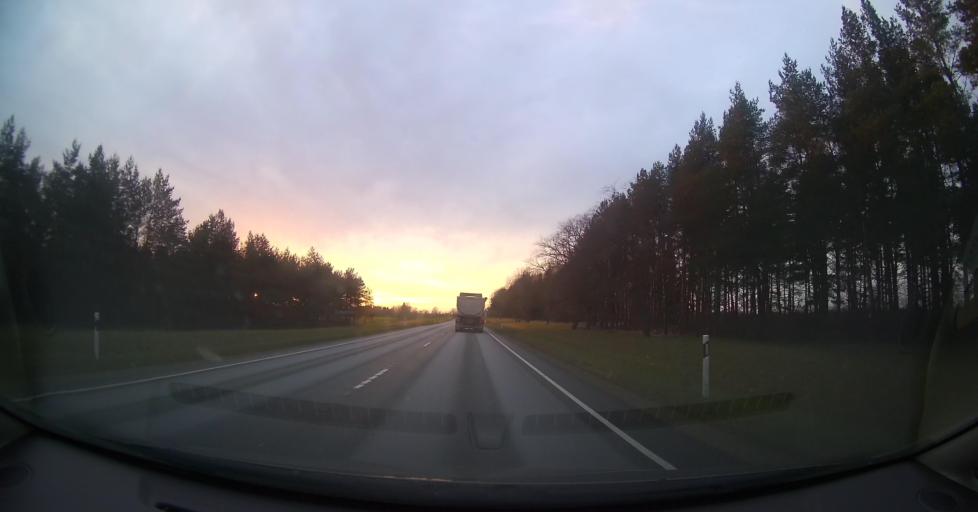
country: EE
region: Ida-Virumaa
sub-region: Aseri vald
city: Aseri
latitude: 59.4369
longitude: 26.7205
